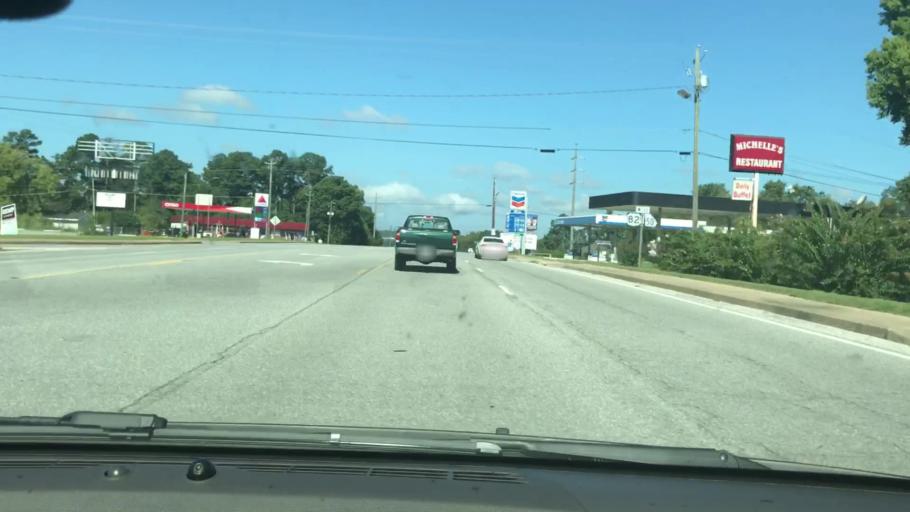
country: US
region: Georgia
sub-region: Quitman County
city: Georgetown
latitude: 31.8880
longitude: -85.1087
